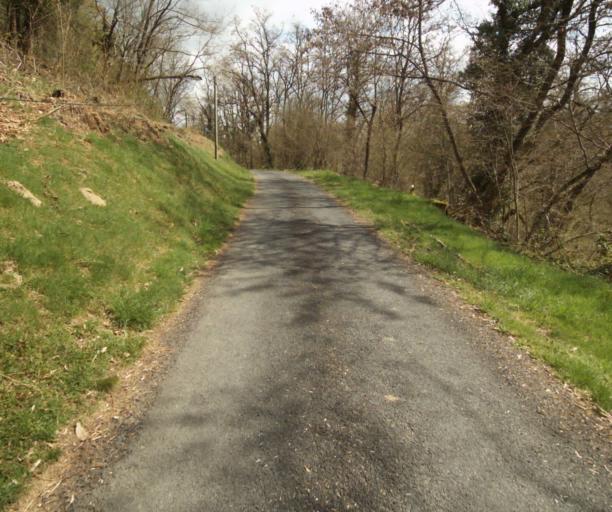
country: FR
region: Limousin
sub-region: Departement de la Correze
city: Laguenne
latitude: 45.2521
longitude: 1.8863
